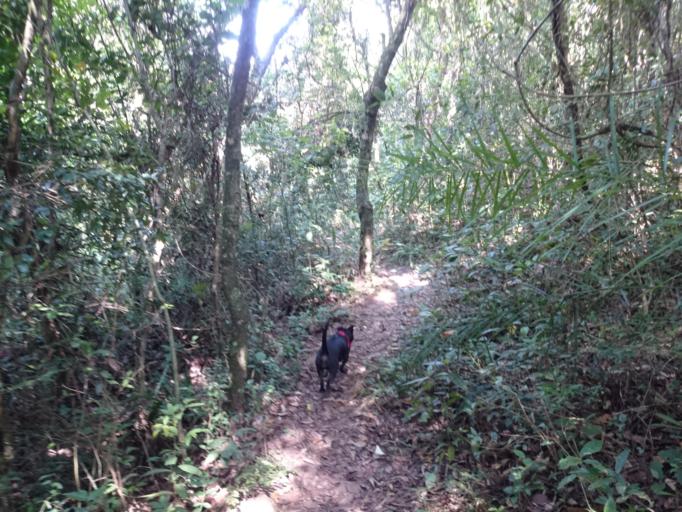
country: BR
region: Sao Paulo
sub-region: Sorocaba
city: Sorocaba
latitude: -23.4739
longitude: -47.4151
